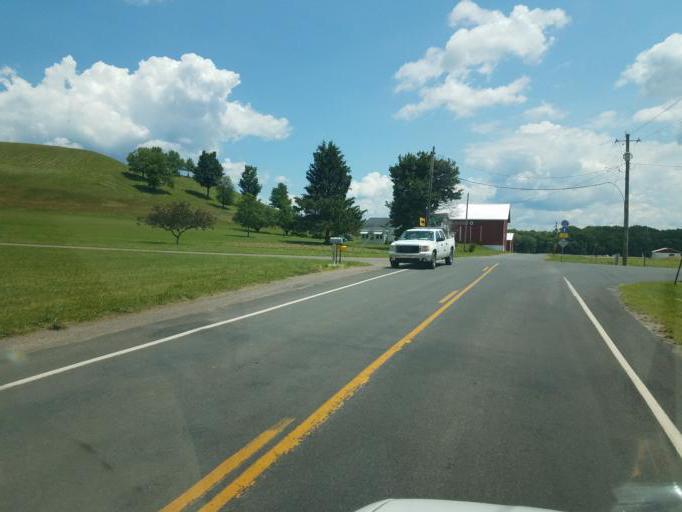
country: US
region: New York
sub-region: Wayne County
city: Clyde
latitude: 43.0613
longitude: -76.8490
